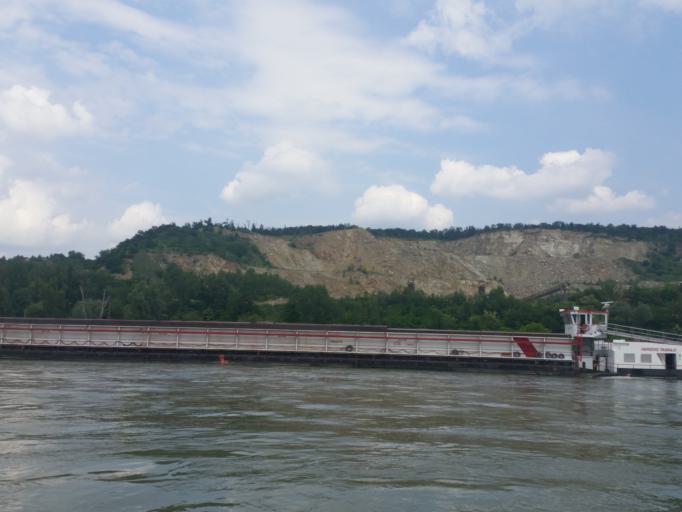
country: AT
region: Lower Austria
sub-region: Politischer Bezirk Bruck an der Leitha
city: Wolfsthal
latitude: 48.1577
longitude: 17.0013
